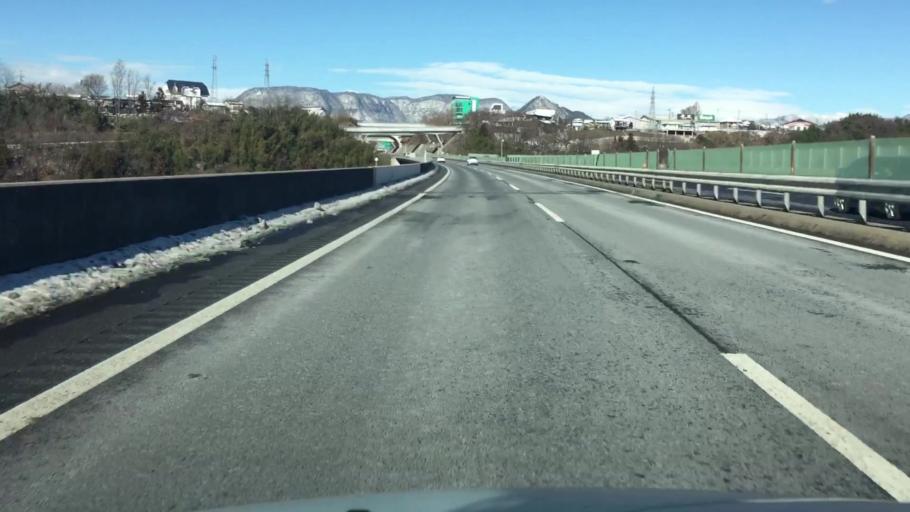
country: JP
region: Gunma
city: Numata
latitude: 36.6498
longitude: 139.0768
